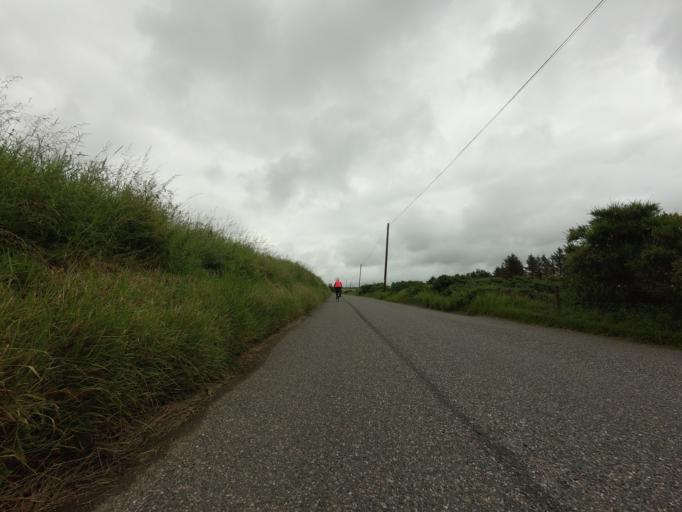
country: GB
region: Scotland
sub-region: Aberdeenshire
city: Turriff
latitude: 57.5359
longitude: -2.3733
